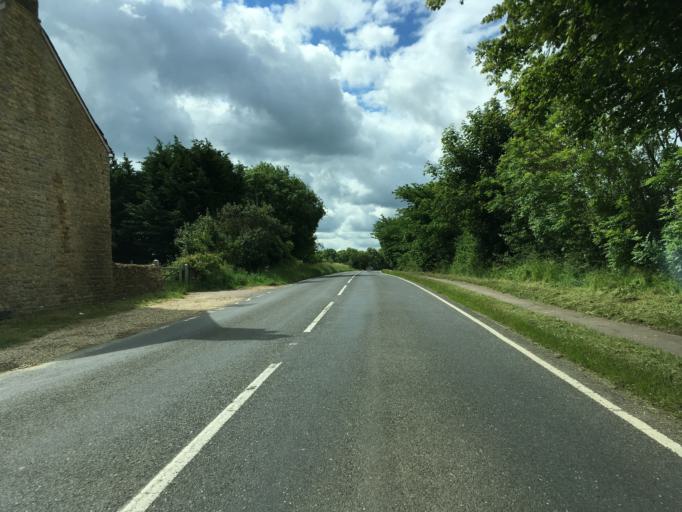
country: GB
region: England
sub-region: Oxfordshire
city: Chipping Norton
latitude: 51.9270
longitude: -1.5413
